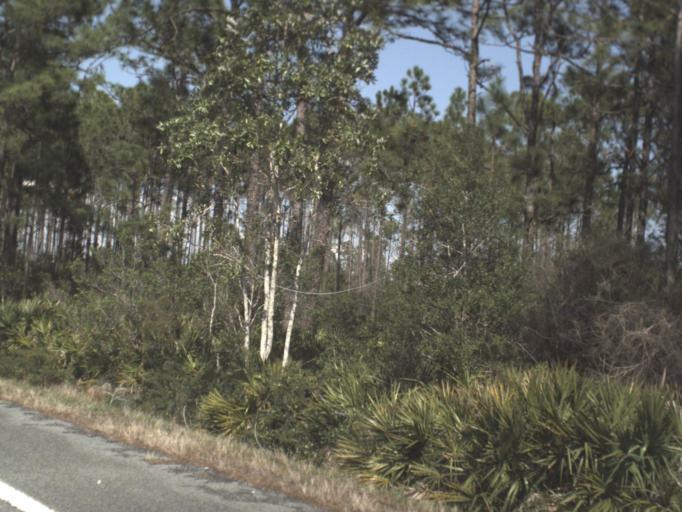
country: US
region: Florida
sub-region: Franklin County
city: Carrabelle
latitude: 29.9418
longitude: -84.5005
